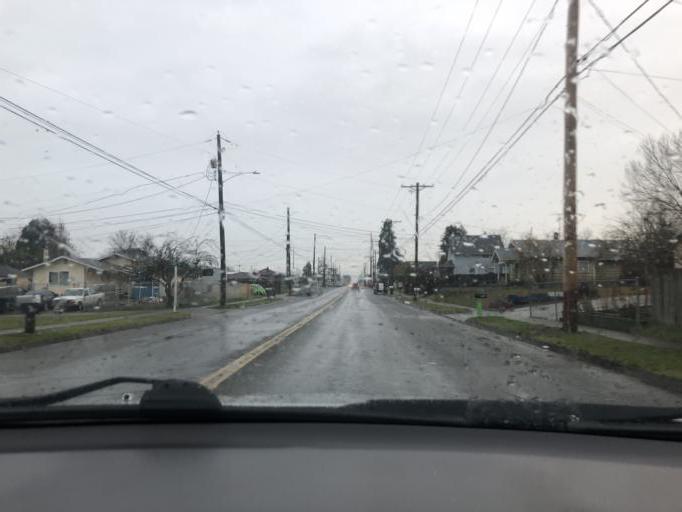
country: US
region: Washington
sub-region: Pierce County
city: Midland
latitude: 47.1960
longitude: -122.4209
